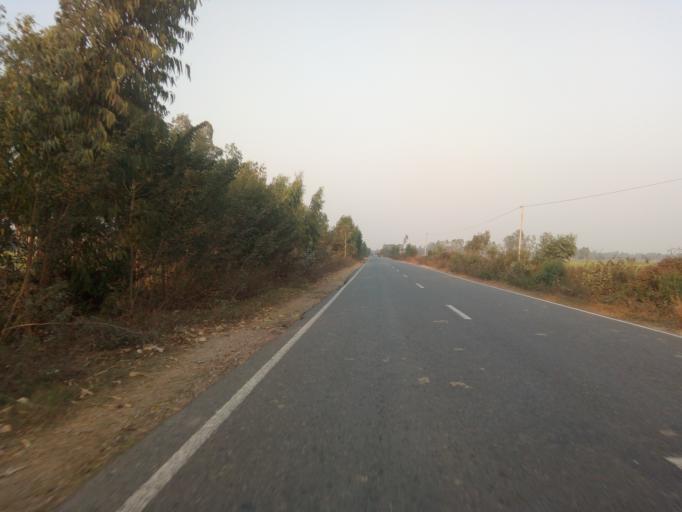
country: BD
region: Rajshahi
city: Bogra
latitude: 24.5807
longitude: 89.2248
